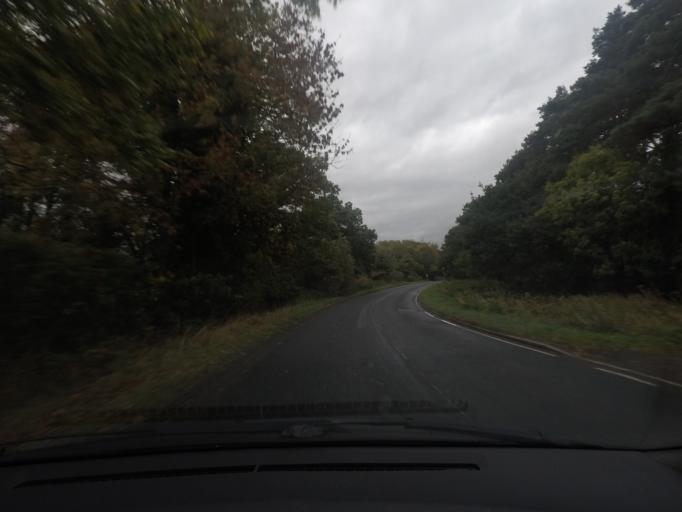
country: GB
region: England
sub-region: City of York
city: Wigginton
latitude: 54.0967
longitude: -1.1107
